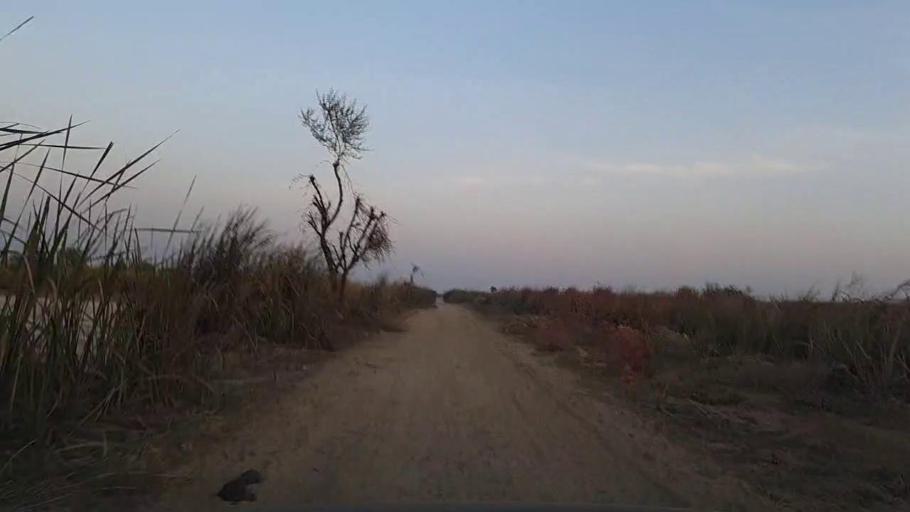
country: PK
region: Sindh
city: Tando Mittha Khan
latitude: 25.9465
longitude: 69.1201
